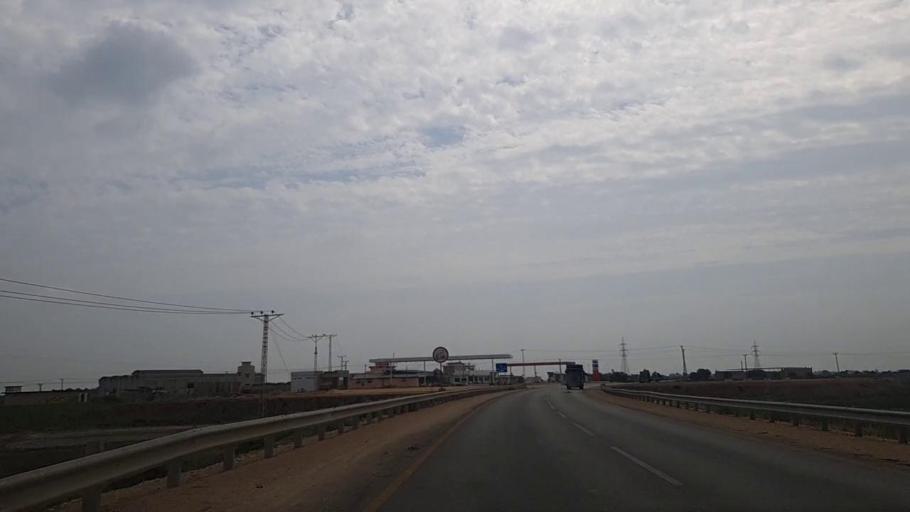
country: PK
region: Sindh
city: Daro Mehar
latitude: 24.6161
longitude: 68.0881
